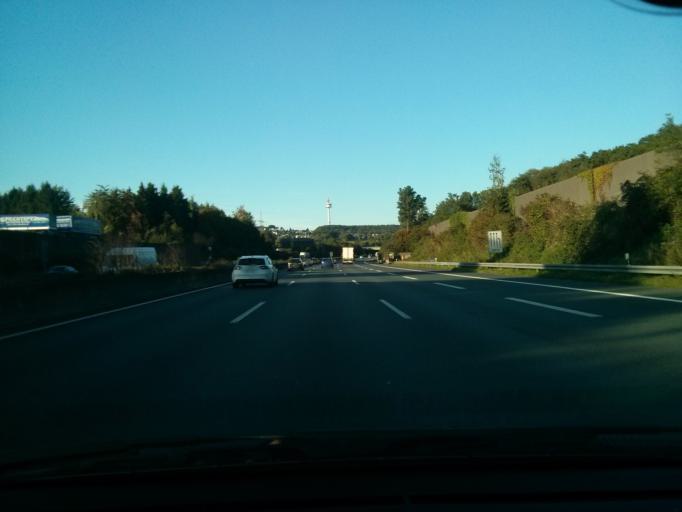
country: DE
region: North Rhine-Westphalia
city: Schwerte
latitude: 51.4438
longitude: 7.5364
